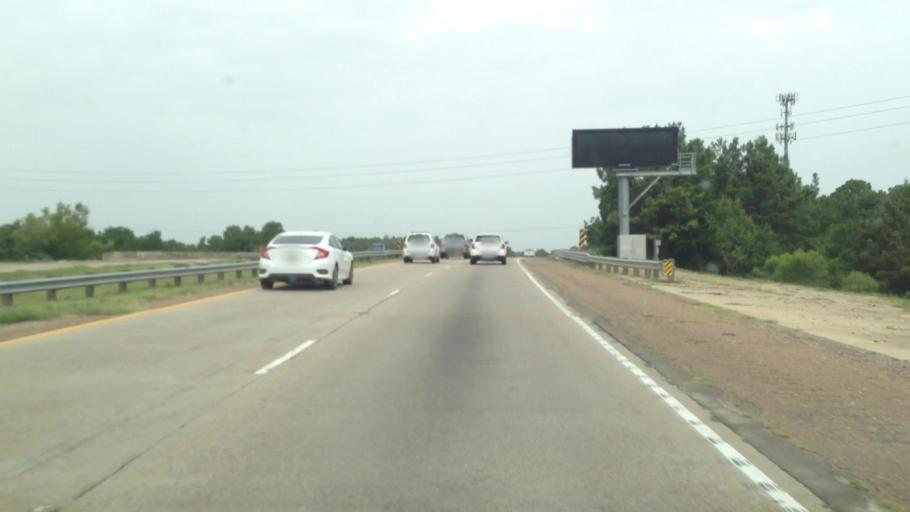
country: US
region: Louisiana
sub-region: Caddo Parish
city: Shreveport
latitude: 32.4189
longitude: -93.8291
